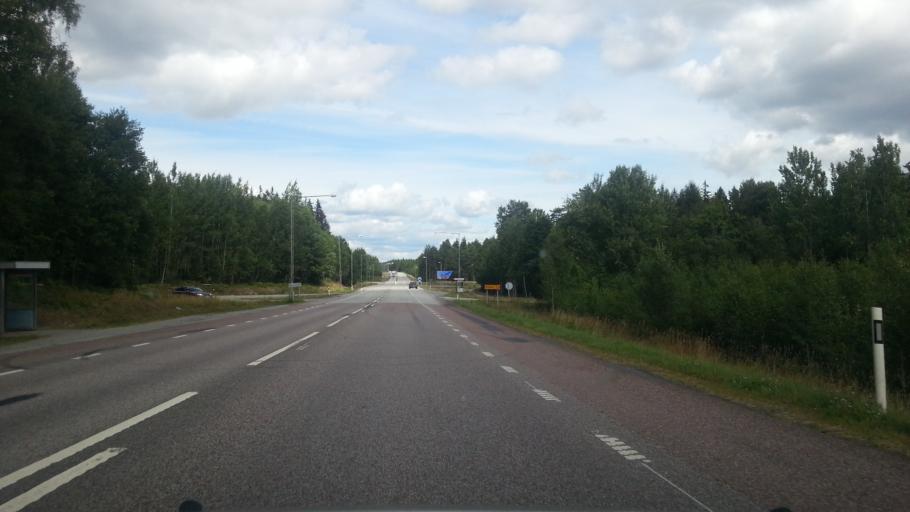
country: SE
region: OErebro
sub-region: Nora Kommun
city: Nora
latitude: 59.4639
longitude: 15.1314
